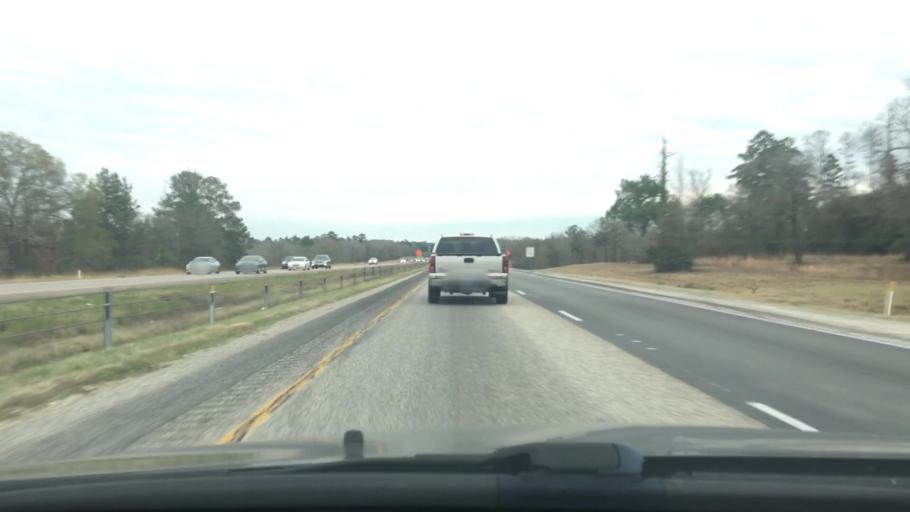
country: US
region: Texas
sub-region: Walker County
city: Huntsville
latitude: 30.7721
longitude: -95.6435
